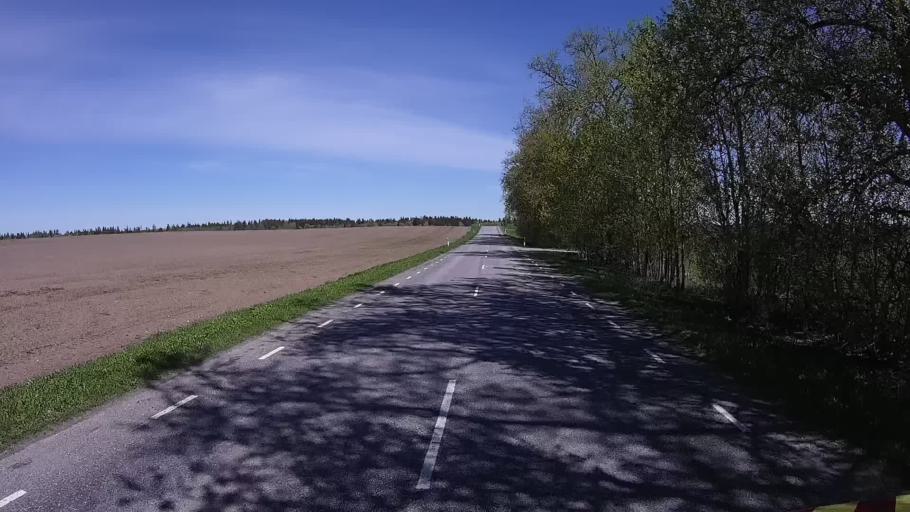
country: EE
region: Raplamaa
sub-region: Kehtna vald
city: Kehtna
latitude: 59.0506
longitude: 25.1262
